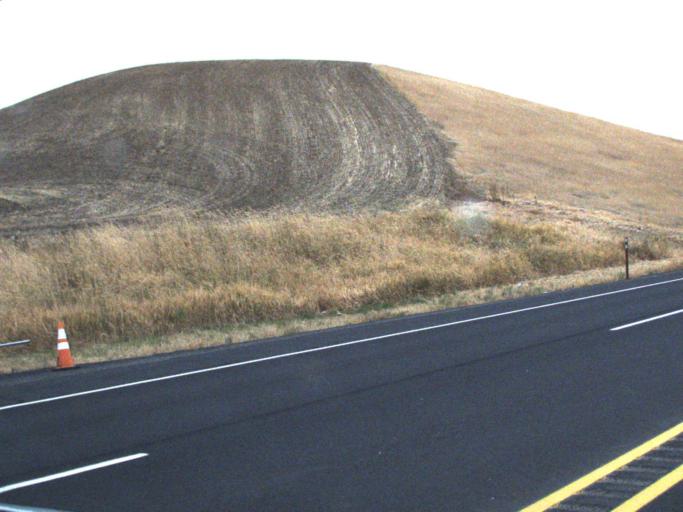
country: US
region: Washington
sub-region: Whitman County
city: Colfax
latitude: 46.9158
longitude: -117.3504
